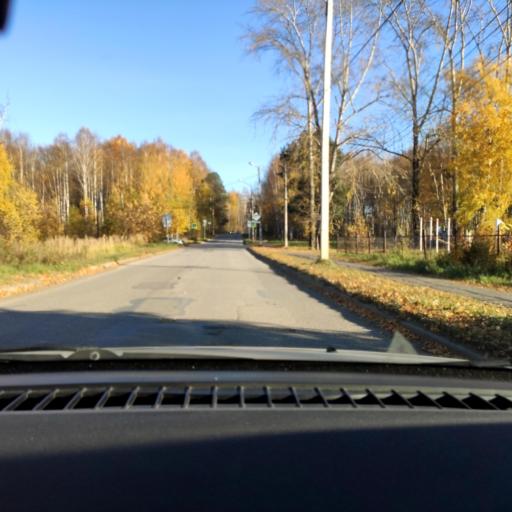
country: RU
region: Perm
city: Perm
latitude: 58.0816
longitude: 56.3607
